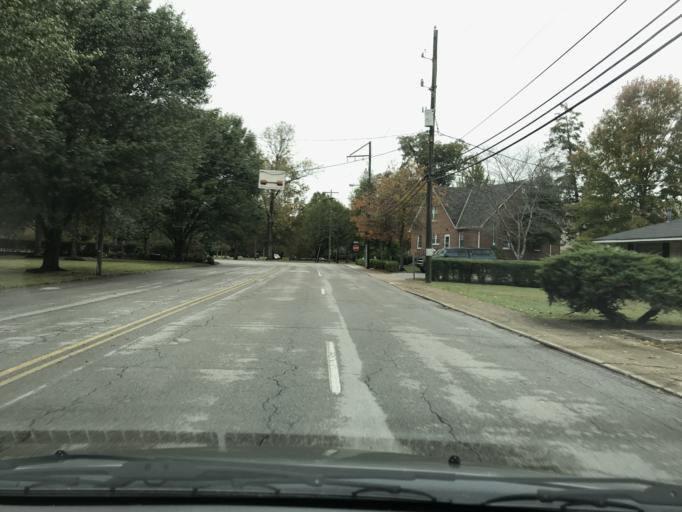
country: US
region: Tennessee
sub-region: Rhea County
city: Dayton
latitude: 35.4860
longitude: -85.0195
